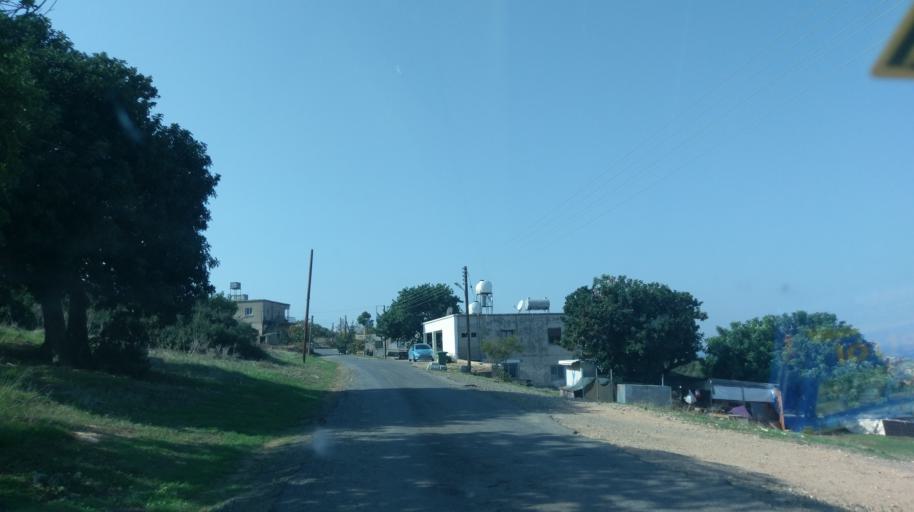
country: CY
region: Lefkosia
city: Morfou
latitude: 35.3833
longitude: 32.9557
